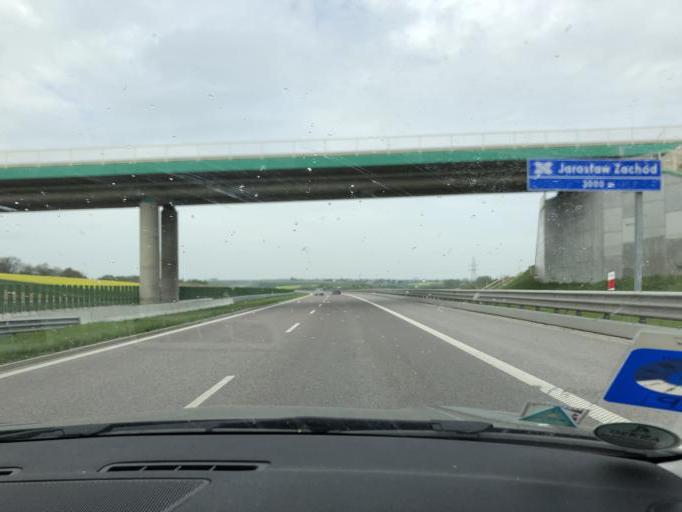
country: PL
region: Subcarpathian Voivodeship
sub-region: Powiat jaroslawski
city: Wierzbna
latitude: 50.0112
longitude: 22.5954
